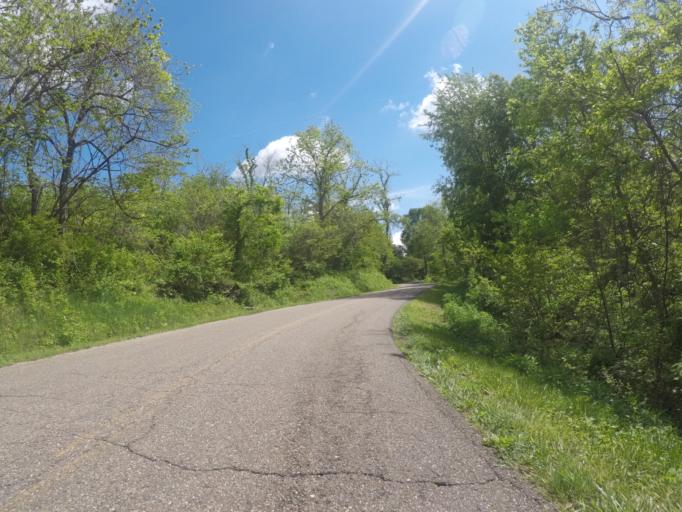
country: US
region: West Virginia
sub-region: Cabell County
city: Huntington
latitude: 38.5450
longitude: -82.4330
